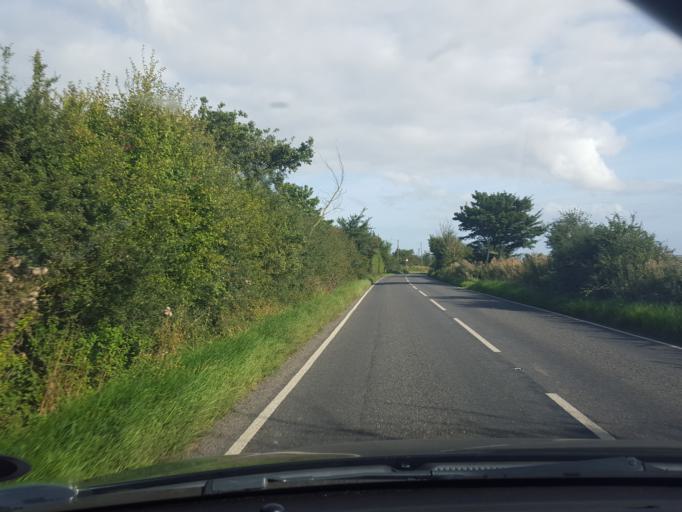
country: GB
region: England
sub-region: Essex
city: Little Clacton
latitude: 51.8940
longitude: 1.1869
